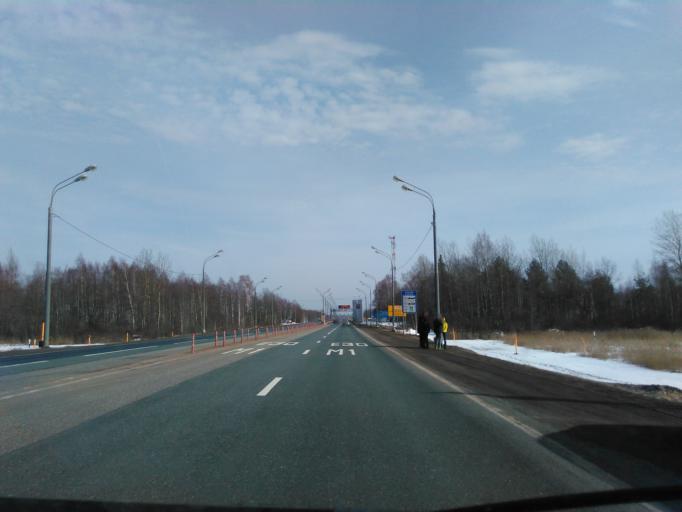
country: RU
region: Smolensk
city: Rudnya
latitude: 54.6907
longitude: 30.9840
